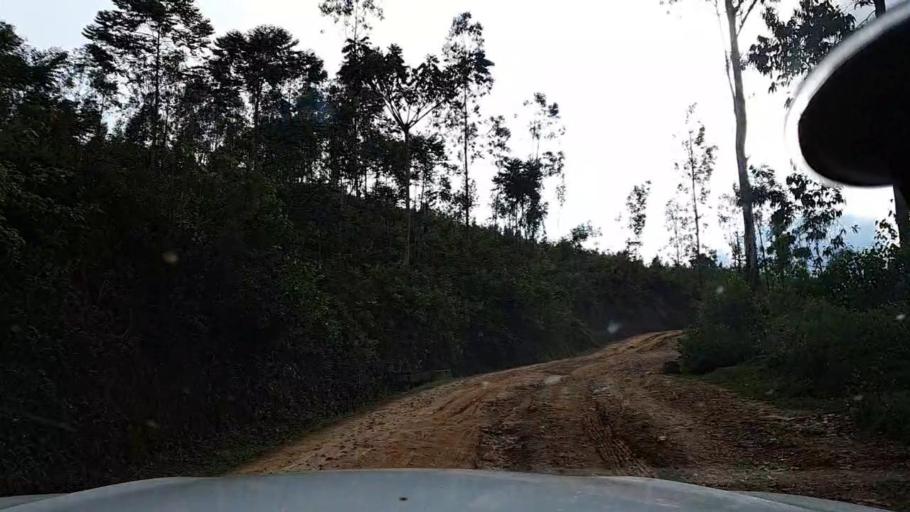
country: RW
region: Southern Province
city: Gitarama
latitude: -2.1683
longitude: 29.5565
